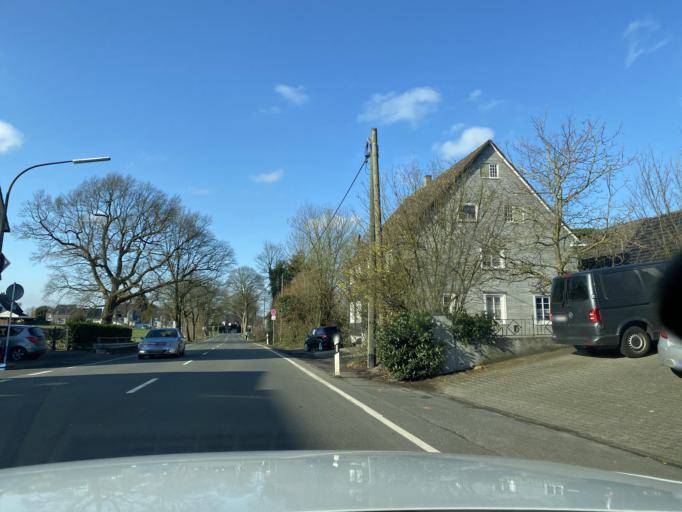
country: DE
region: North Rhine-Westphalia
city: Wermelskirchen
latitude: 51.1094
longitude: 7.1713
